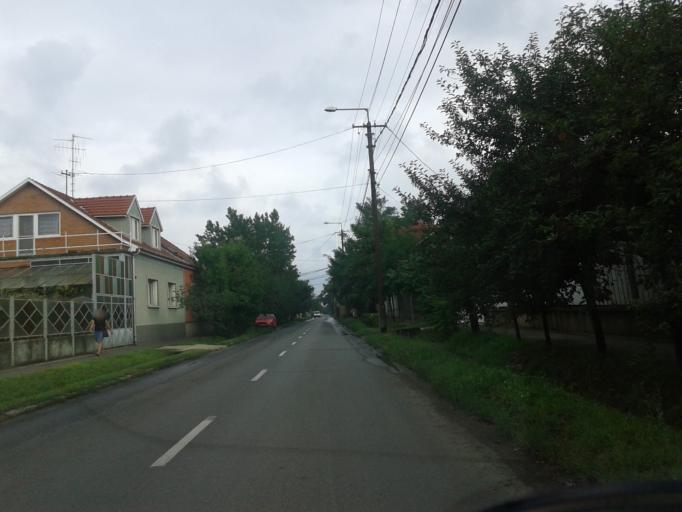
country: HU
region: Csongrad
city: Szeged
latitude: 46.2668
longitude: 20.1781
